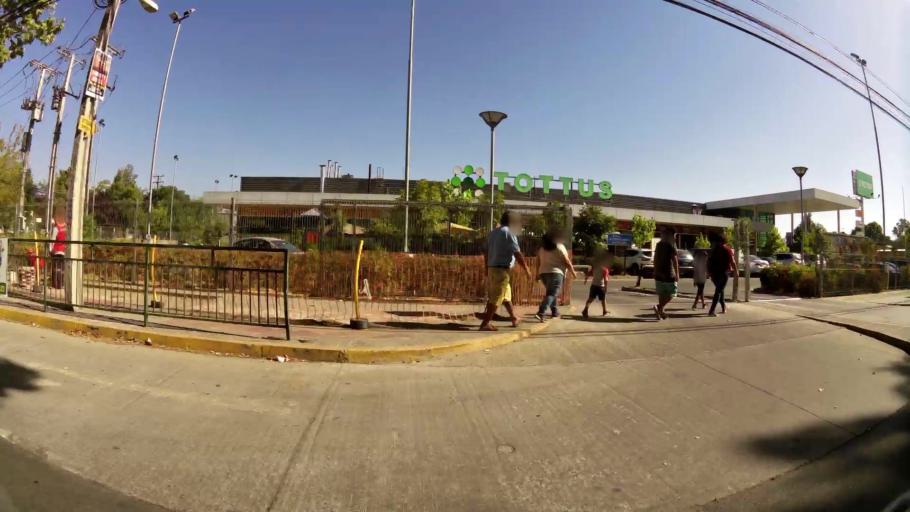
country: CL
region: Maule
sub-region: Provincia de Talca
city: Talca
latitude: -35.4231
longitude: -71.6546
